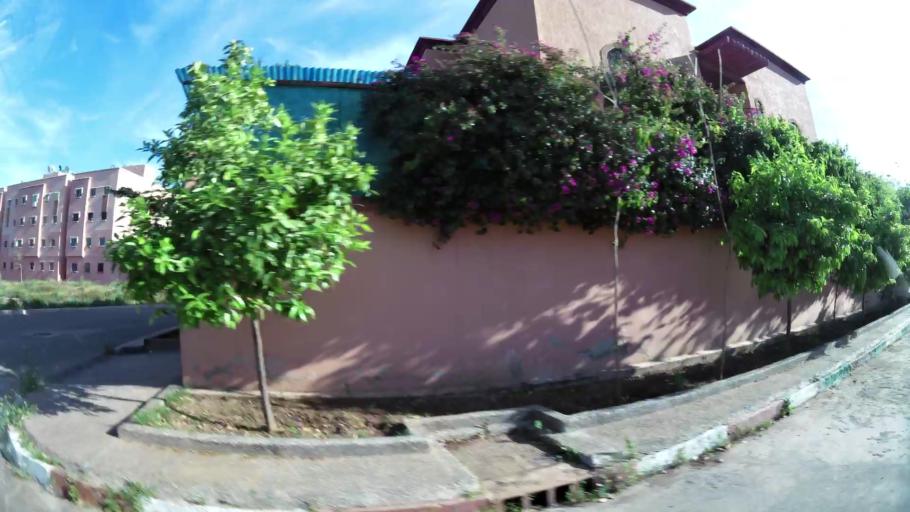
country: MA
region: Marrakech-Tensift-Al Haouz
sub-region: Marrakech
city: Marrakesh
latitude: 31.6911
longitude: -8.0633
